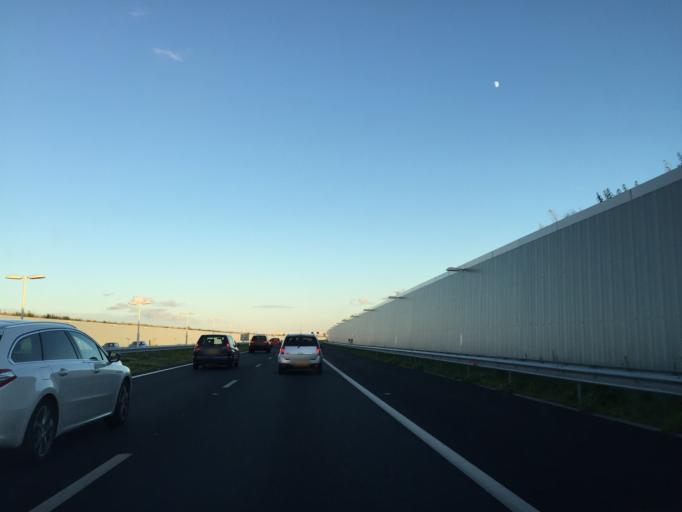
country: NL
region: South Holland
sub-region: Gemeente Delft
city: Delft
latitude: 51.9705
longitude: 4.3407
